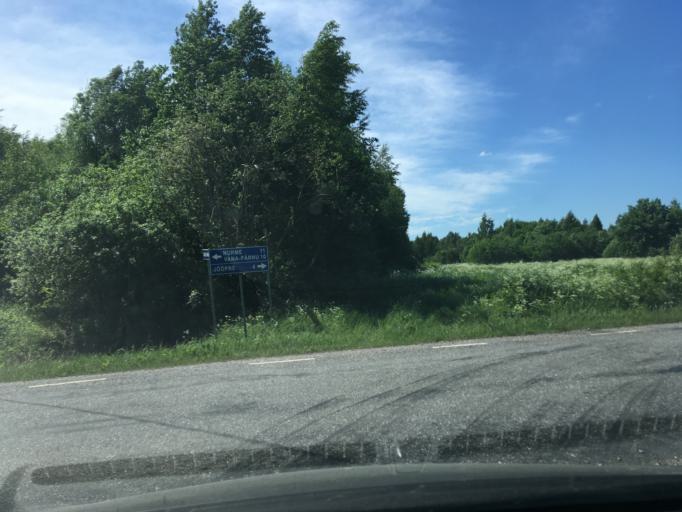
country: EE
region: Paernumaa
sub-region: Audru vald
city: Audru
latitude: 58.4548
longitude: 24.3809
